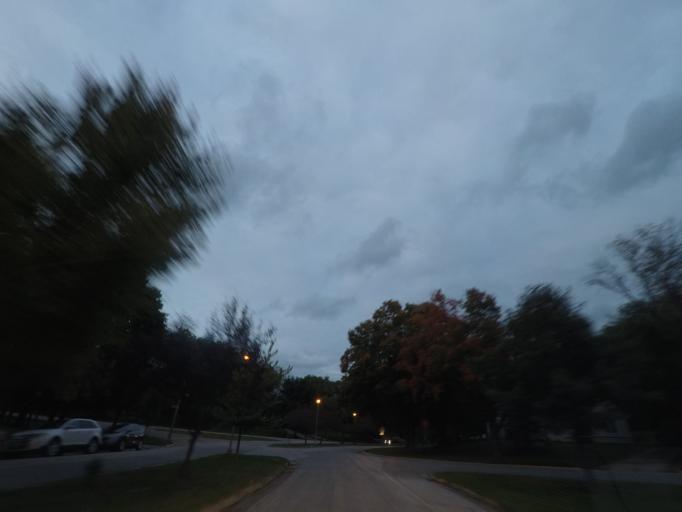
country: US
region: Iowa
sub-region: Story County
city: Ames
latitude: 42.0175
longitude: -93.6418
